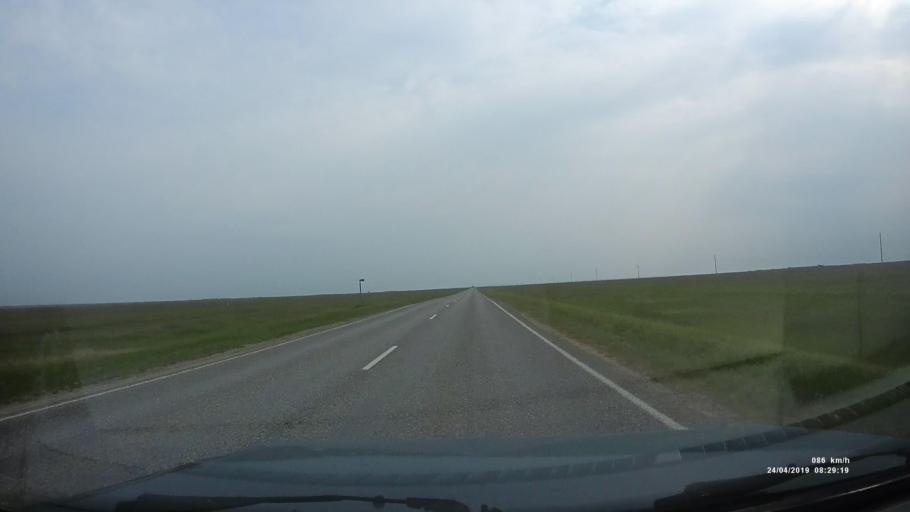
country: RU
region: Kalmykiya
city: Priyutnoye
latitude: 46.1518
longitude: 43.8300
